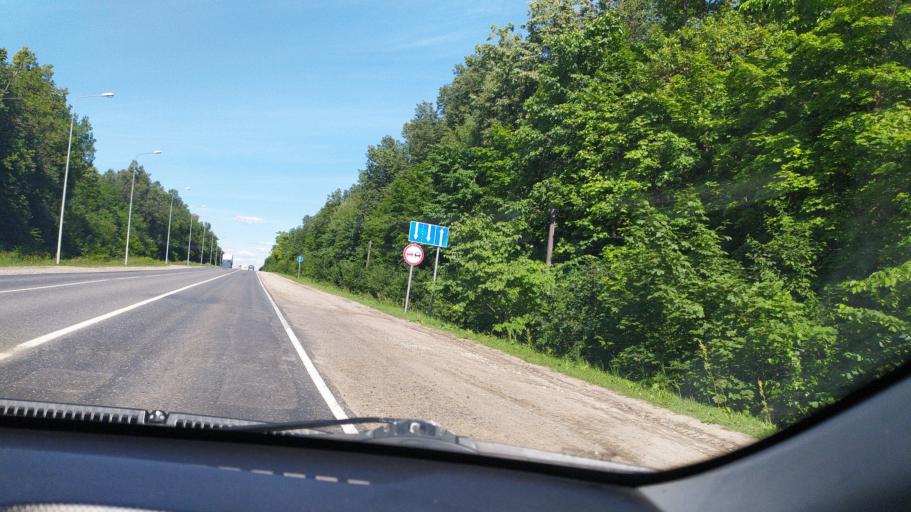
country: RU
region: Chuvashia
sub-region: Cheboksarskiy Rayon
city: Cheboksary
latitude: 56.0919
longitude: 47.2504
